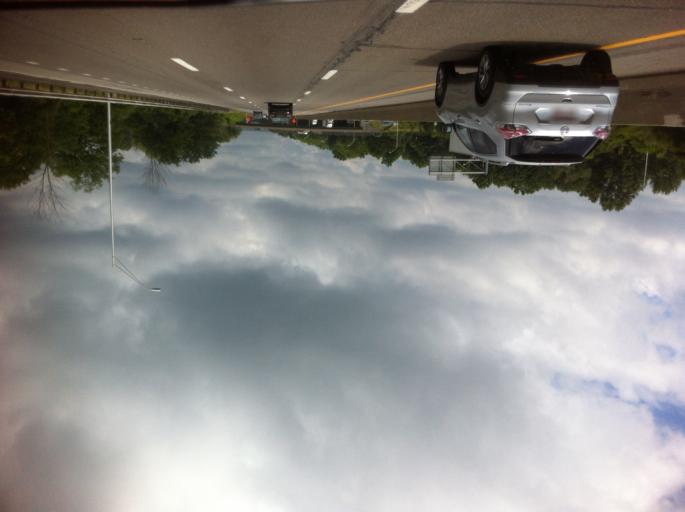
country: US
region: Ohio
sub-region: Lorain County
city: North Ridgeville
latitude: 41.3793
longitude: -82.0020
